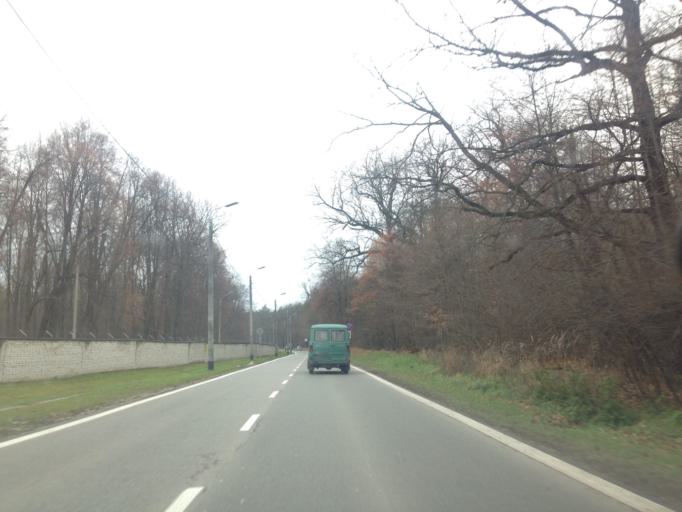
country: PL
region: Masovian Voivodeship
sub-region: Warszawa
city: Rembertow
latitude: 52.2512
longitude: 21.1480
